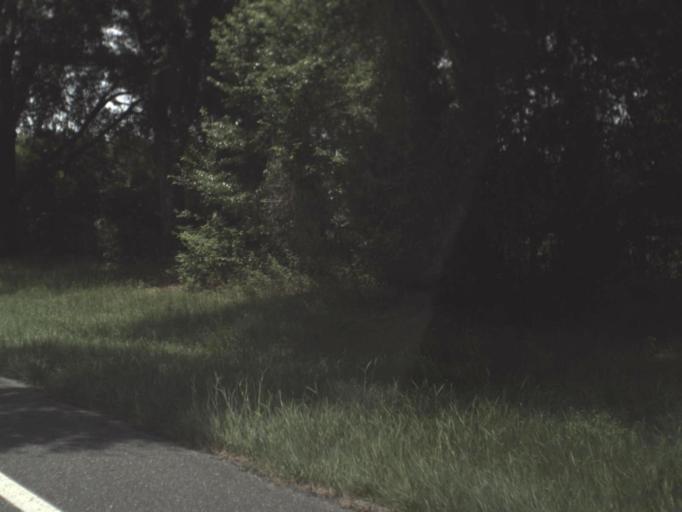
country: US
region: Florida
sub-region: Alachua County
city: Newberry
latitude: 29.5944
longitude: -82.5666
